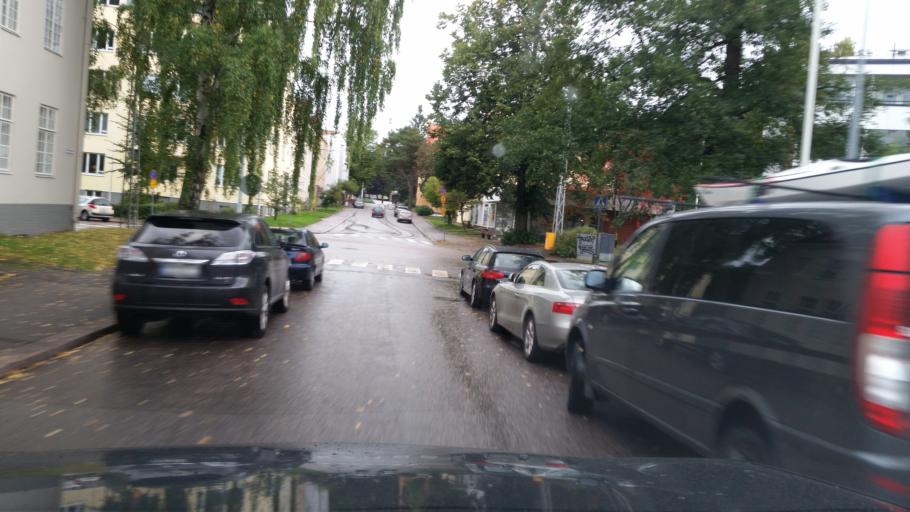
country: FI
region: Uusimaa
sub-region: Helsinki
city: Teekkarikylae
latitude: 60.1940
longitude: 24.8739
